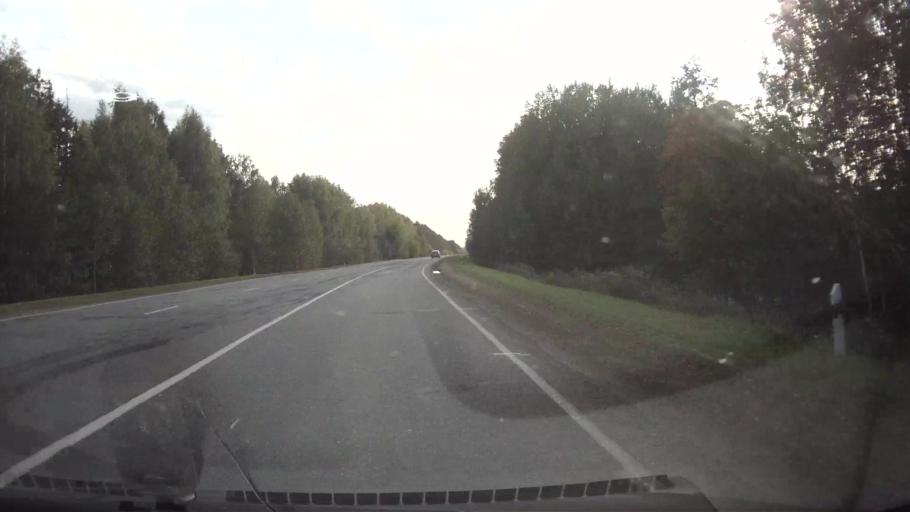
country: RU
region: Mariy-El
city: Sovetskiy
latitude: 56.7927
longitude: 48.6801
